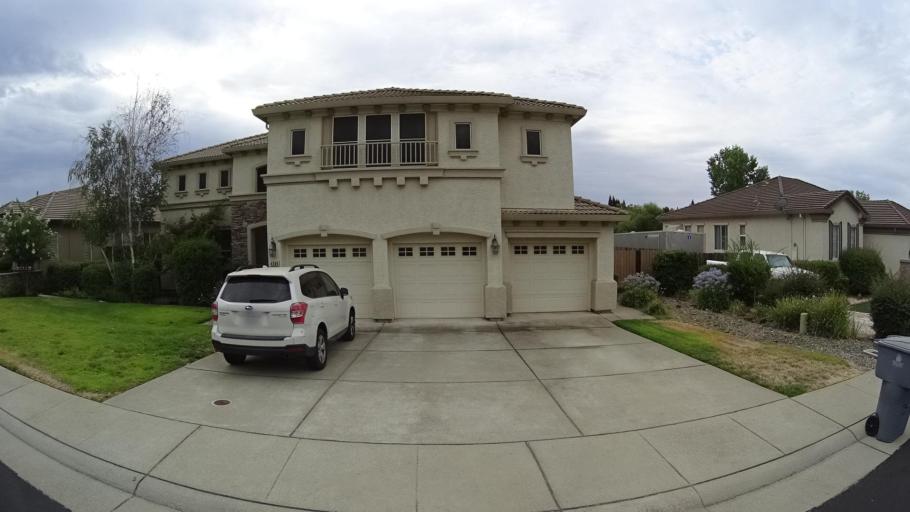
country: US
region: California
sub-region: Placer County
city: Rocklin
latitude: 38.7731
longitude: -121.2240
